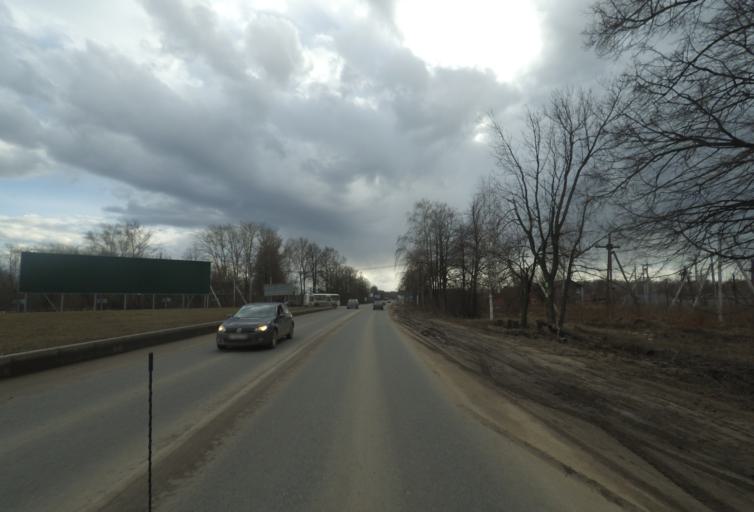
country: RU
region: Nizjnij Novgorod
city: Afonino
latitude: 56.2270
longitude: 44.0953
